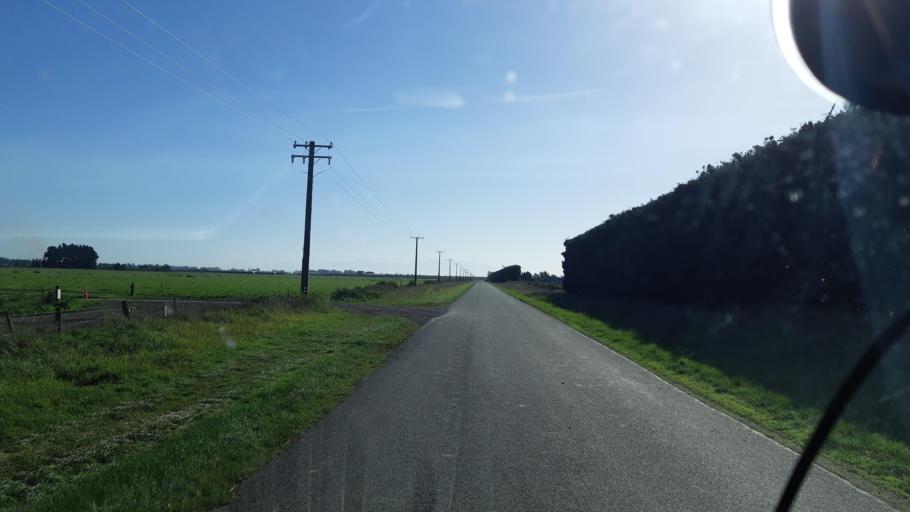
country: NZ
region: Canterbury
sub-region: Selwyn District
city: Burnham
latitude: -43.6331
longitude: 172.2181
